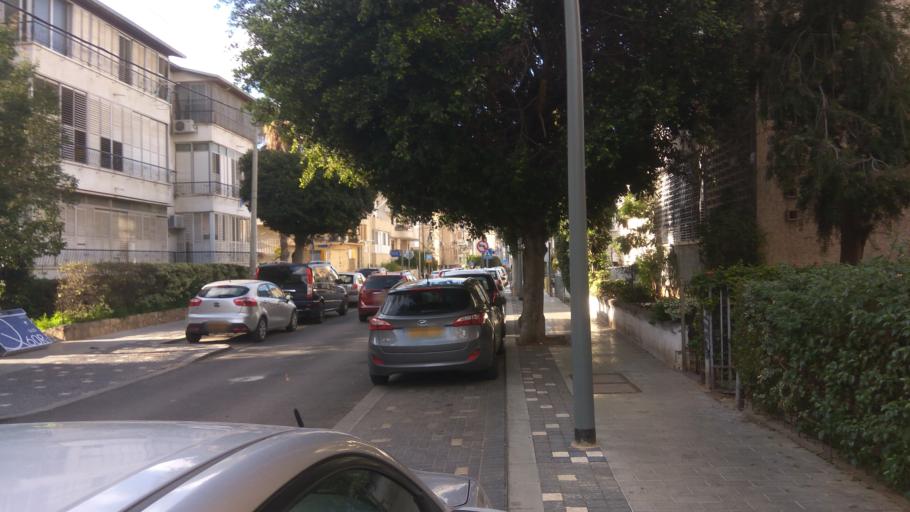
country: IL
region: Central District
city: Rishon LeZiyyon
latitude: 31.9678
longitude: 34.8063
